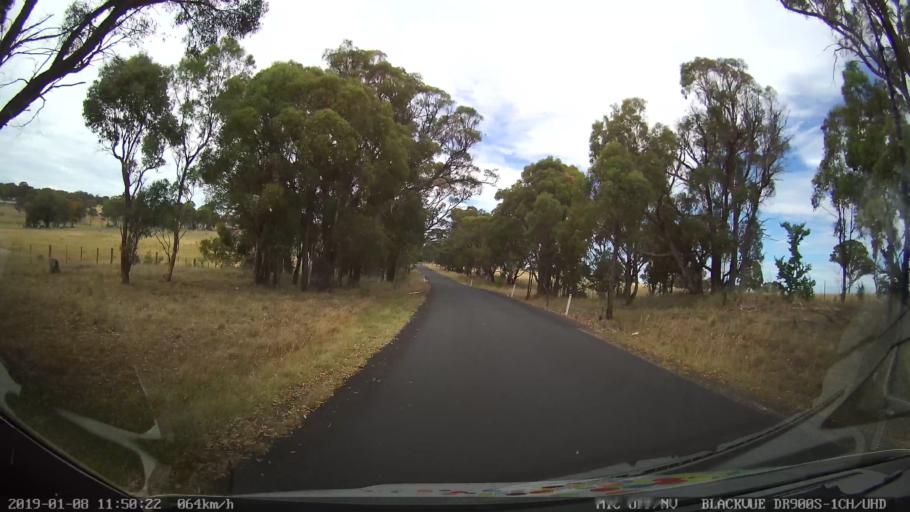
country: AU
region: New South Wales
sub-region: Armidale Dumaresq
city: Armidale
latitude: -30.3820
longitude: 151.5573
